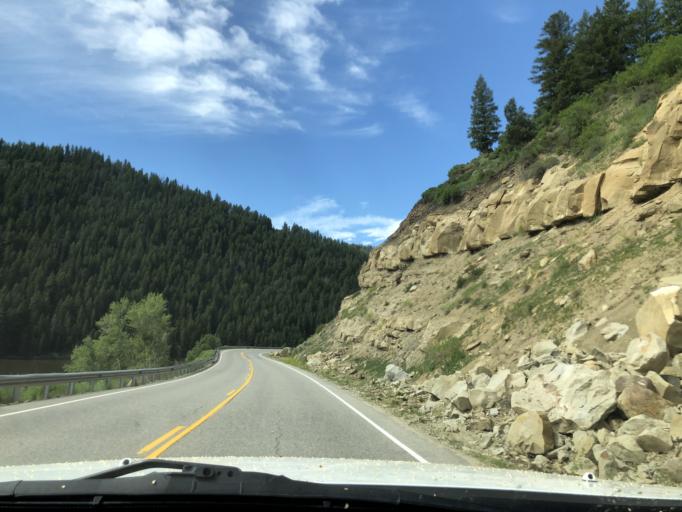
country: US
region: Colorado
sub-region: Delta County
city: Paonia
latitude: 38.9449
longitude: -107.3496
